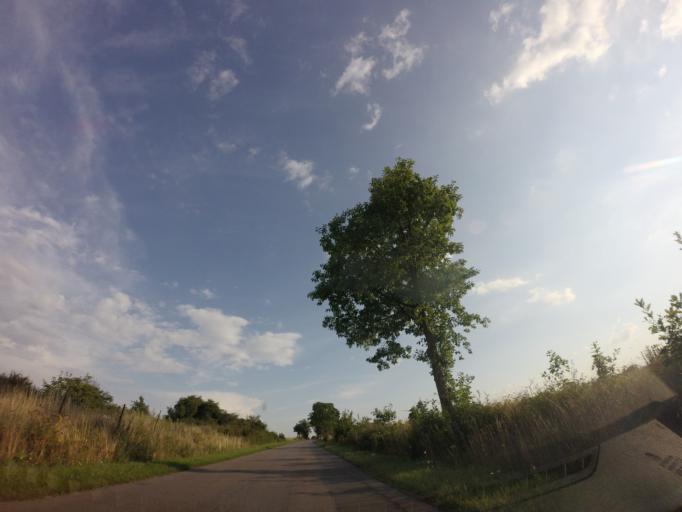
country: PL
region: Lublin Voivodeship
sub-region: Powiat lubartowski
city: Michow
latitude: 51.5167
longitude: 22.3109
